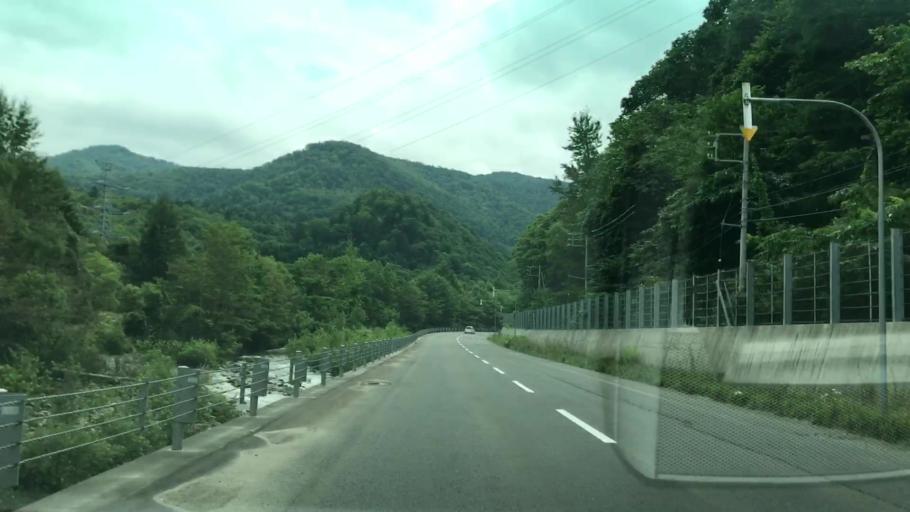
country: JP
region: Hokkaido
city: Yoichi
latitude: 43.0379
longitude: 140.8609
